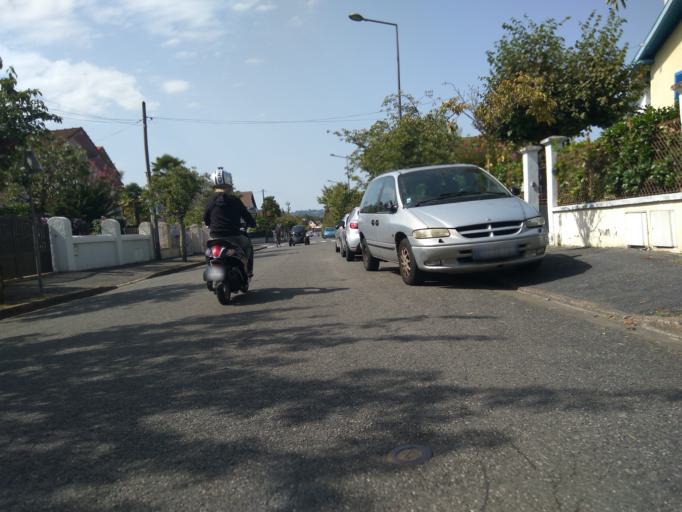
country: FR
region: Aquitaine
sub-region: Departement des Pyrenees-Atlantiques
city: Bizanos
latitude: 43.2930
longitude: -0.3542
